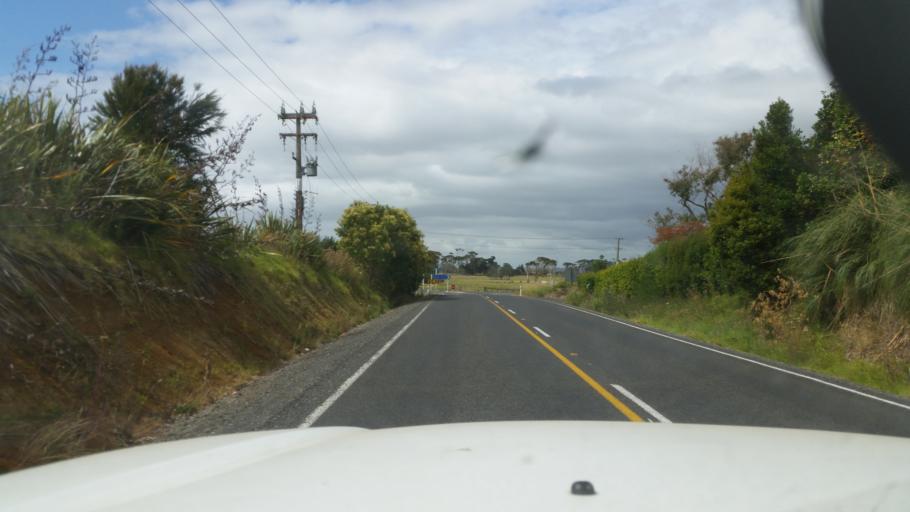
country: NZ
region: Northland
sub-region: Far North District
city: Ahipara
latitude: -35.1730
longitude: 173.1795
